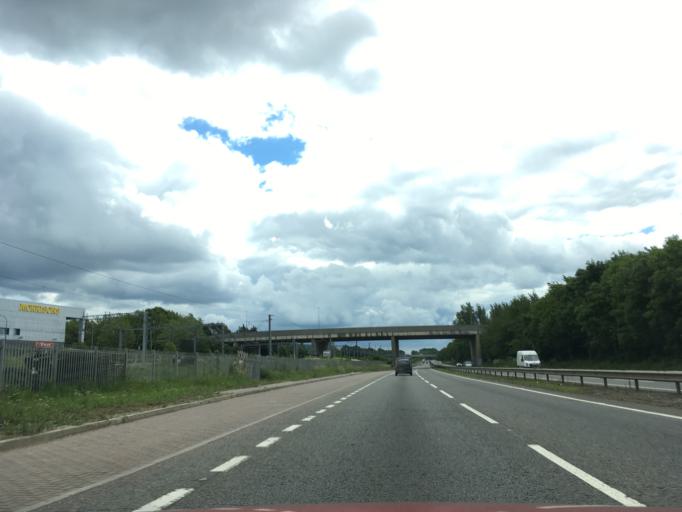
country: GB
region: England
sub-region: Milton Keynes
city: Loughton
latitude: 52.0318
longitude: -0.7726
